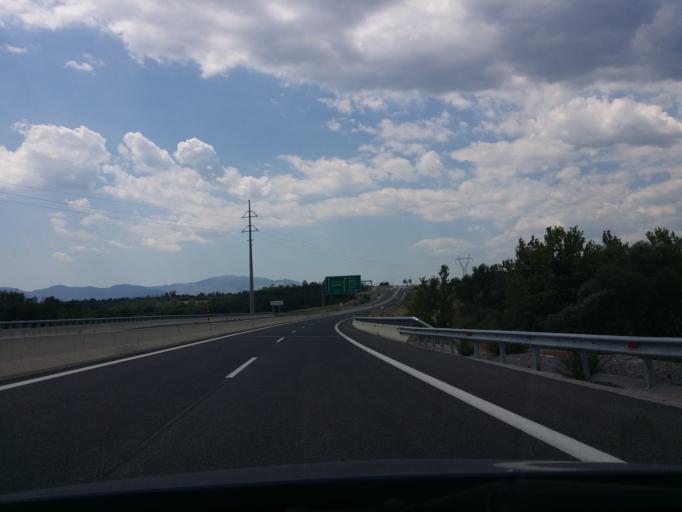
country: GR
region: Peloponnese
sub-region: Nomos Arkadias
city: Megalopoli
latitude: 37.3537
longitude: 22.1542
